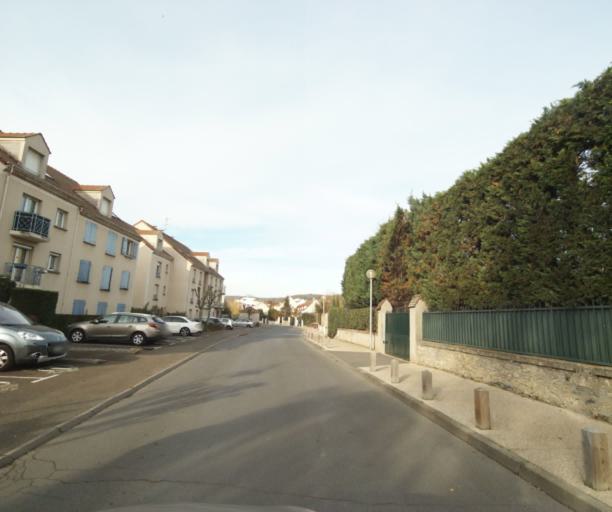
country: FR
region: Ile-de-France
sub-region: Departement des Yvelines
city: Triel-sur-Seine
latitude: 48.9744
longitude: 2.0047
